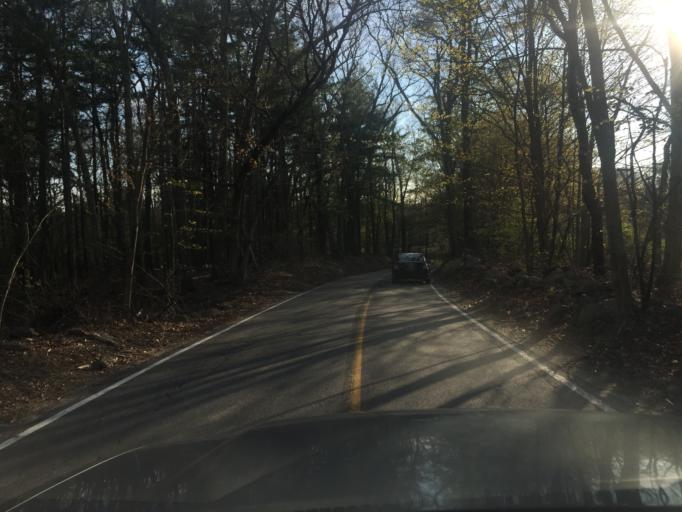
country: US
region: Massachusetts
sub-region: Middlesex County
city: Sherborn
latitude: 42.2267
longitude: -71.3511
